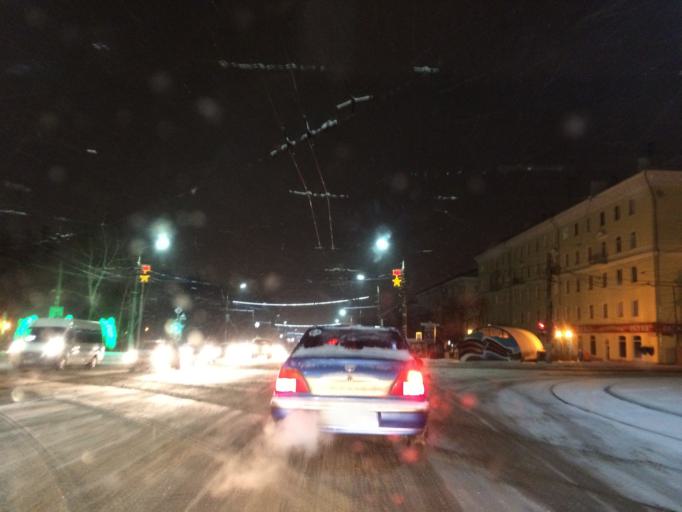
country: RU
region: Tula
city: Mendeleyevskiy
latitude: 54.1665
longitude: 37.5884
